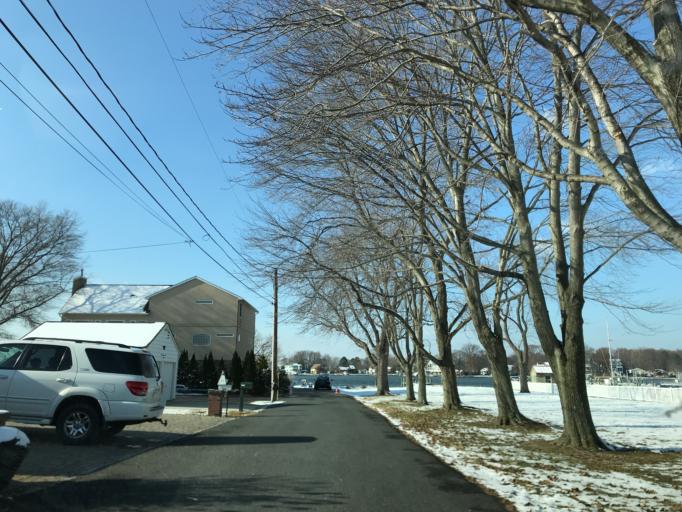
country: US
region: Maryland
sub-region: Baltimore County
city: Bowleys Quarters
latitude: 39.3090
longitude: -76.3874
